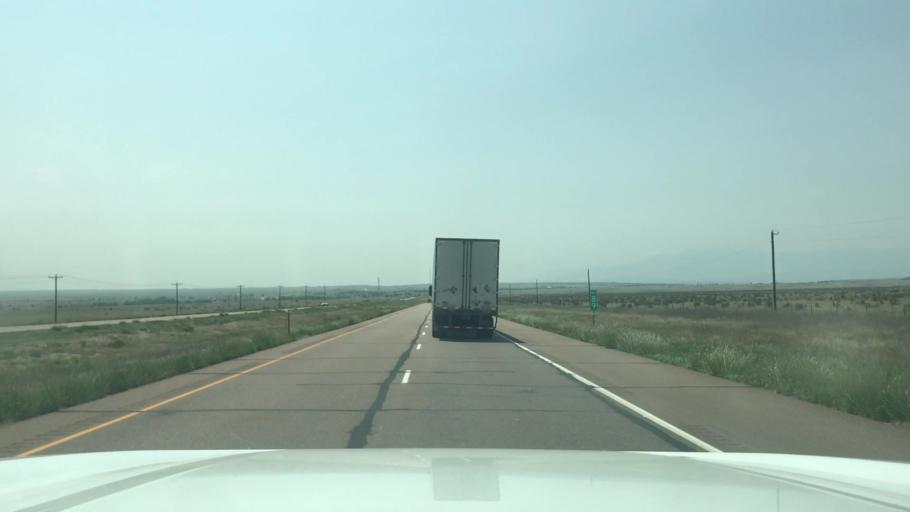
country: US
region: Colorado
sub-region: Pueblo County
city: Pueblo
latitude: 38.1423
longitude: -104.6601
